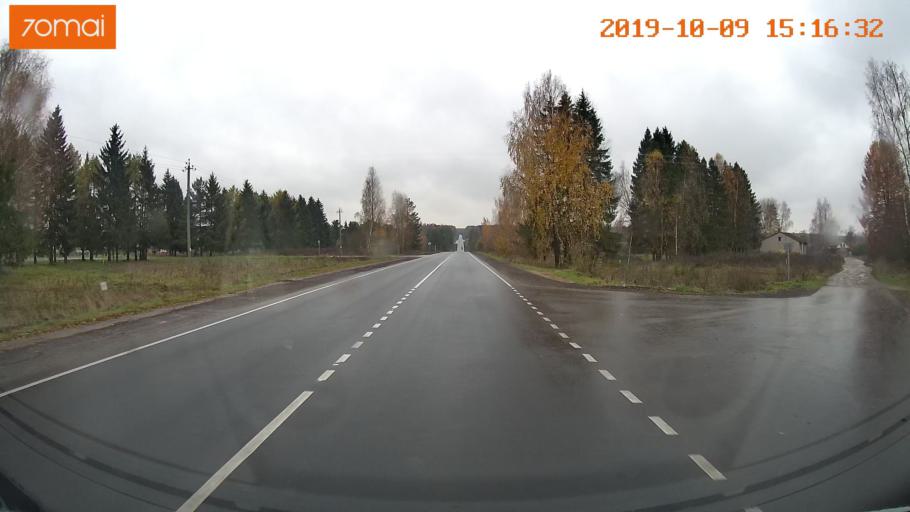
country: RU
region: Kostroma
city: Susanino
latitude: 58.1094
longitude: 41.5857
